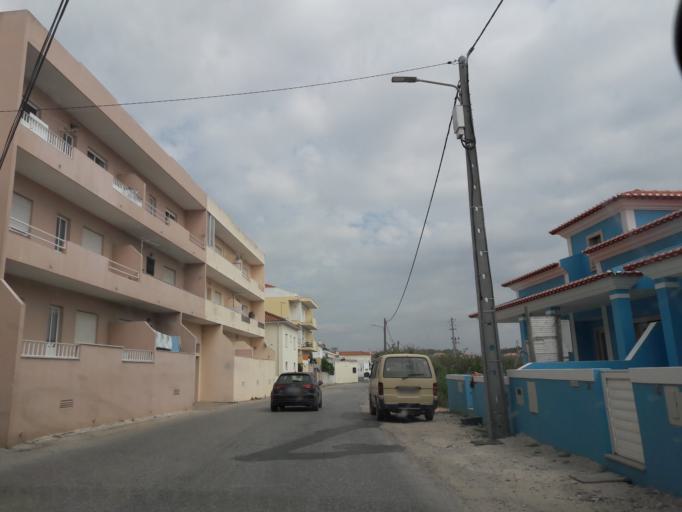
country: PT
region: Leiria
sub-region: Peniche
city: Atouguia da Baleia
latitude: 39.3627
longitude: -9.3133
